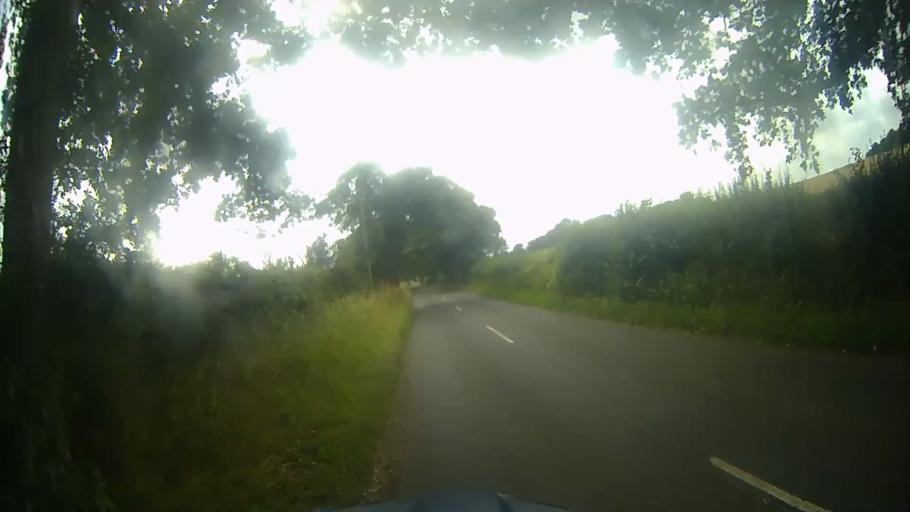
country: GB
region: England
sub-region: Hampshire
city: Overton
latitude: 51.2677
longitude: -1.3082
